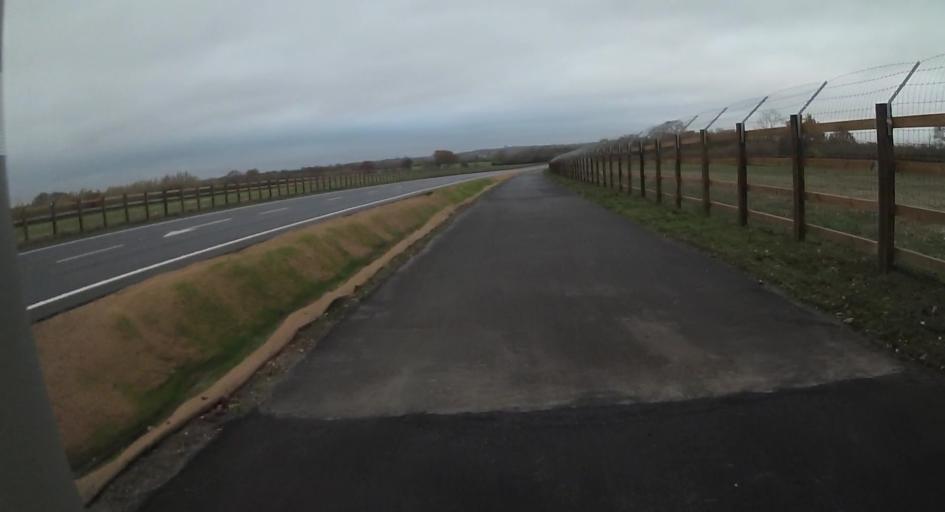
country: GB
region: England
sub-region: West Berkshire
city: Arborfield
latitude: 51.3935
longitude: -0.9176
